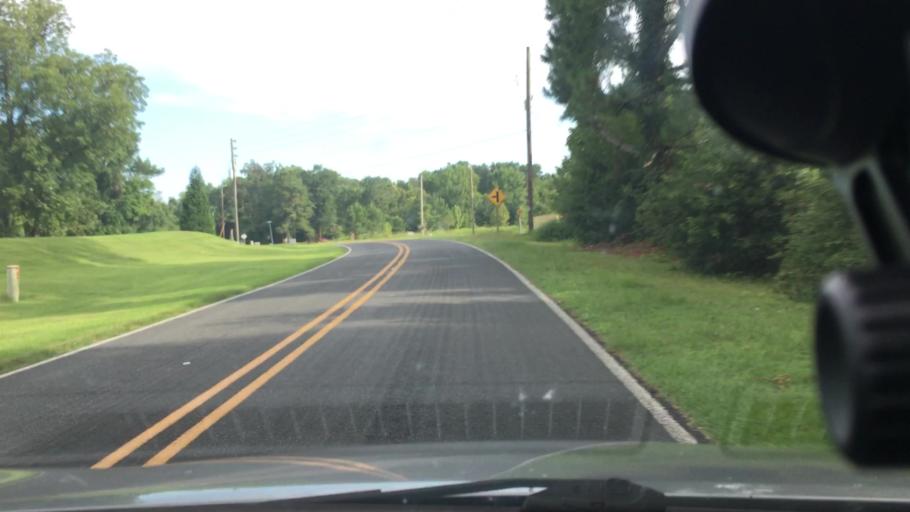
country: US
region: North Carolina
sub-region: Craven County
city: New Bern
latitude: 35.1849
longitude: -77.0583
